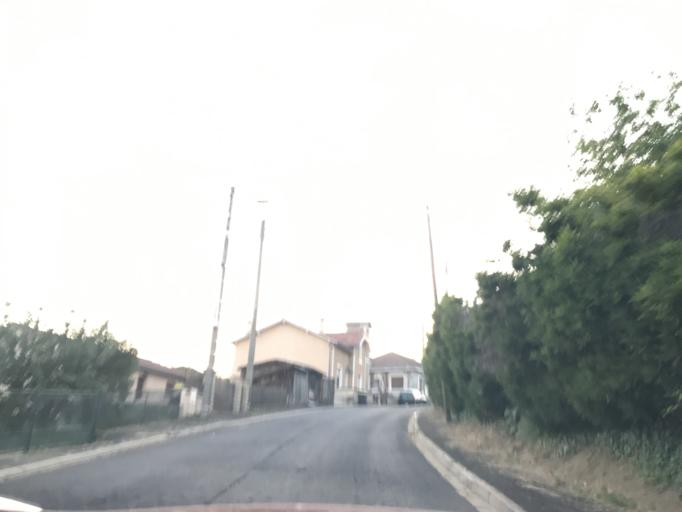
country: FR
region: Auvergne
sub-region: Departement du Puy-de-Dome
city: Saint-Remy-sur-Durolle
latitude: 45.8852
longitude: 3.5914
